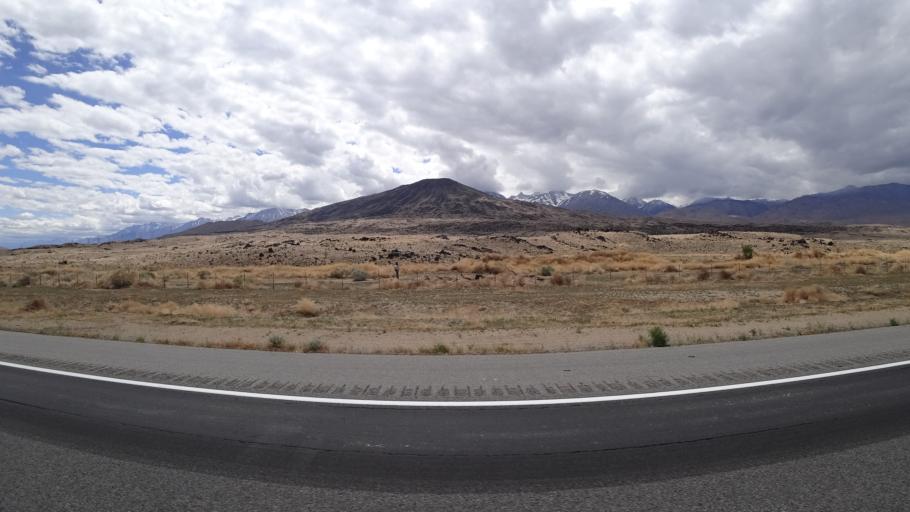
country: US
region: California
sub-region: Inyo County
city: Big Pine
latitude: 37.1301
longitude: -118.2698
